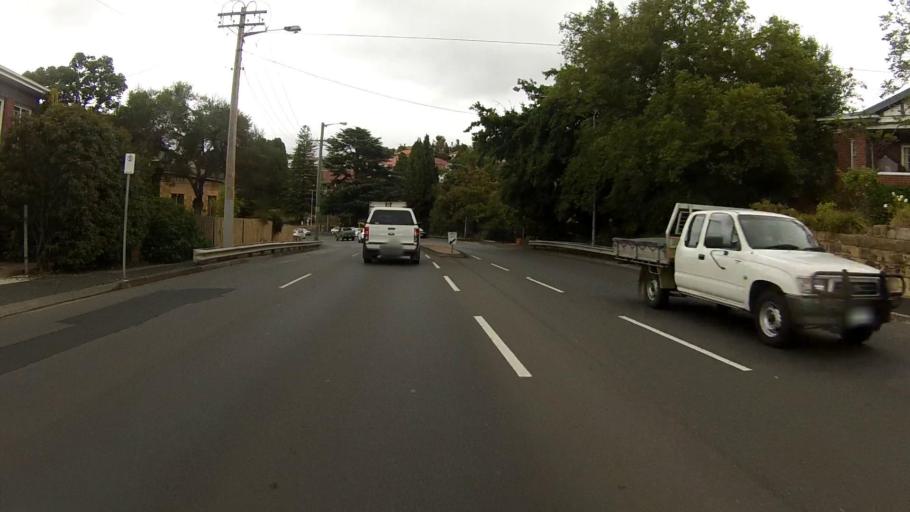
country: AU
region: Tasmania
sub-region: Hobart
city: New Town
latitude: -42.8690
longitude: 147.3118
